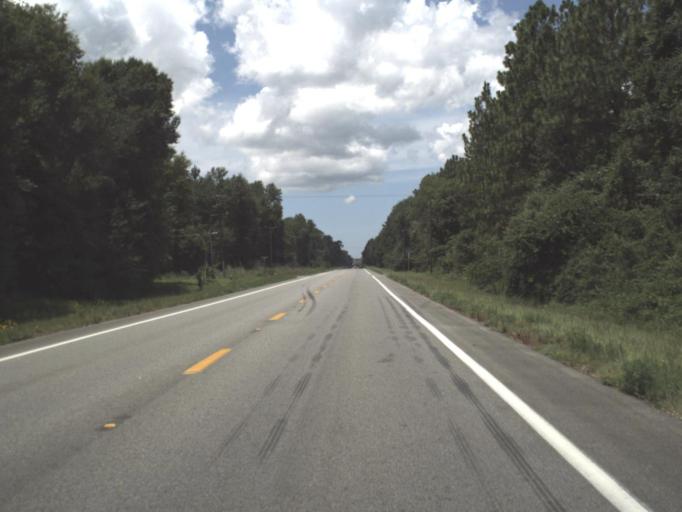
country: US
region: Florida
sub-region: Taylor County
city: Perry
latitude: 30.0997
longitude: -83.6214
